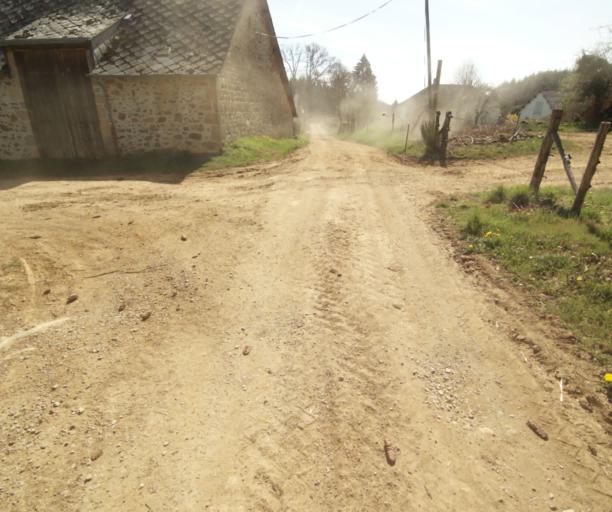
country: FR
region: Limousin
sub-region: Departement de la Correze
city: Seilhac
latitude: 45.4060
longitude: 1.7745
